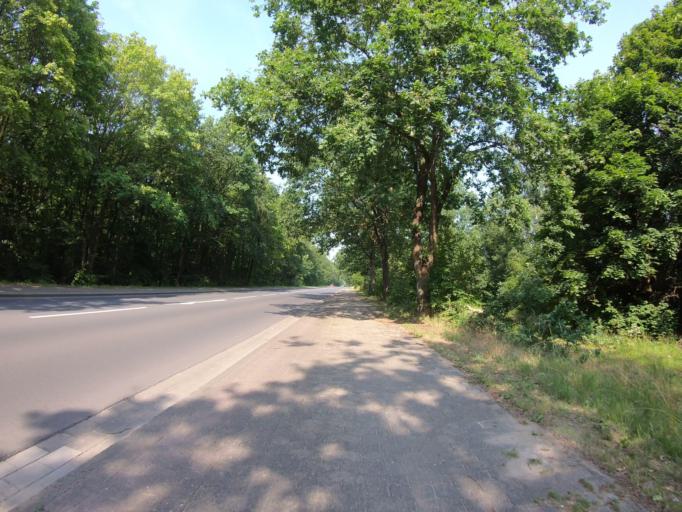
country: DE
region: Lower Saxony
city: Gifhorn
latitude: 52.4610
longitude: 10.5699
